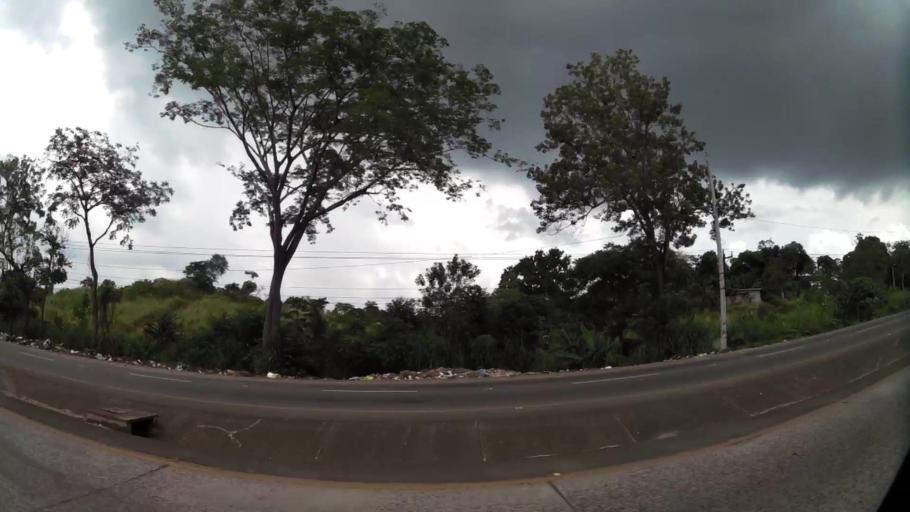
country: PA
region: Panama
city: Cabra Numero Uno
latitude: 9.1006
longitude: -79.3340
